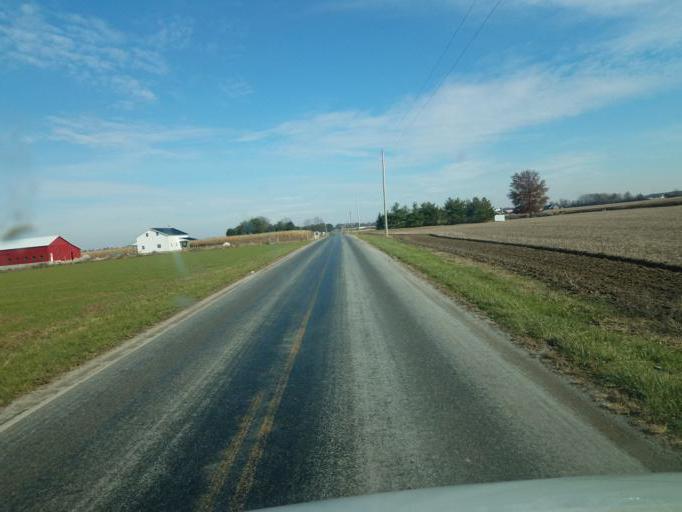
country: US
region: Ohio
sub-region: Hardin County
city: Kenton
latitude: 40.5633
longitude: -83.4353
